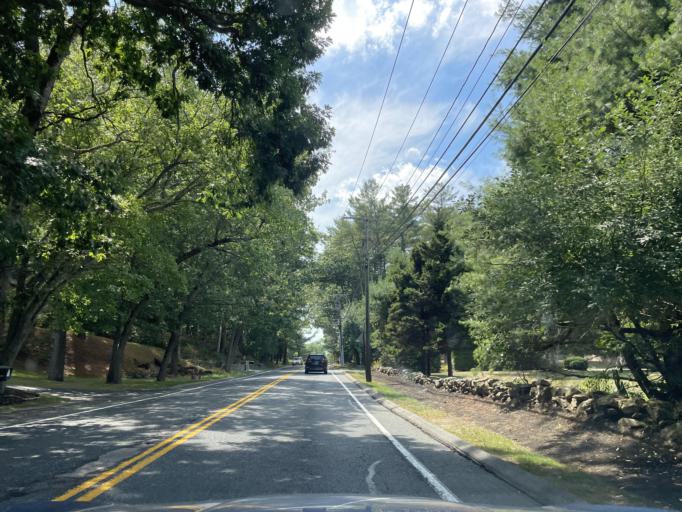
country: US
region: Massachusetts
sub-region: Middlesex County
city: Natick
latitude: 42.2608
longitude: -71.3282
